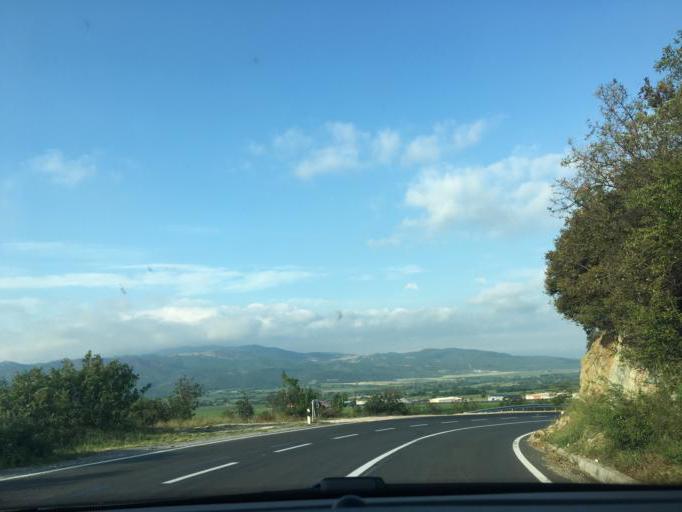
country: MK
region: Valandovo
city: Valandovo
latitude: 41.3187
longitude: 22.5961
